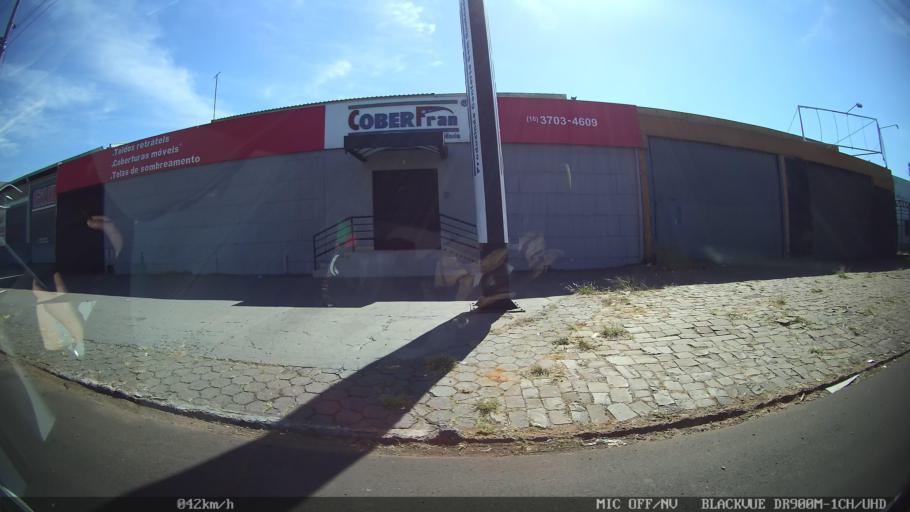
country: BR
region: Sao Paulo
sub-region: Franca
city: Franca
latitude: -20.5551
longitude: -47.4389
